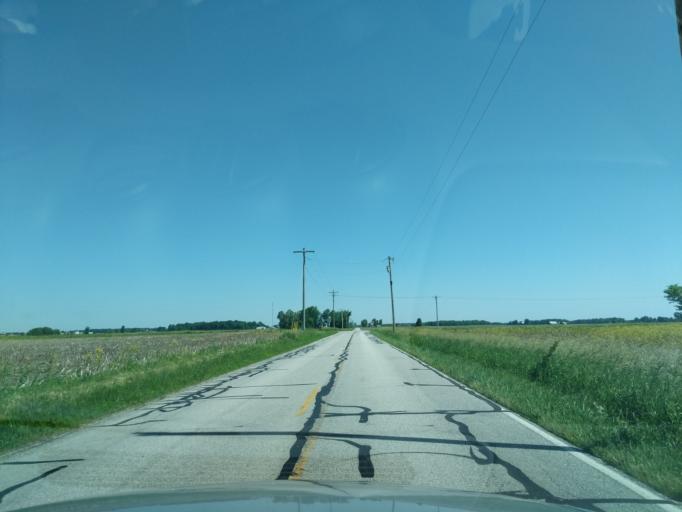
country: US
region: Indiana
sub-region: Huntington County
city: Warren
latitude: 40.6811
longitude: -85.5067
